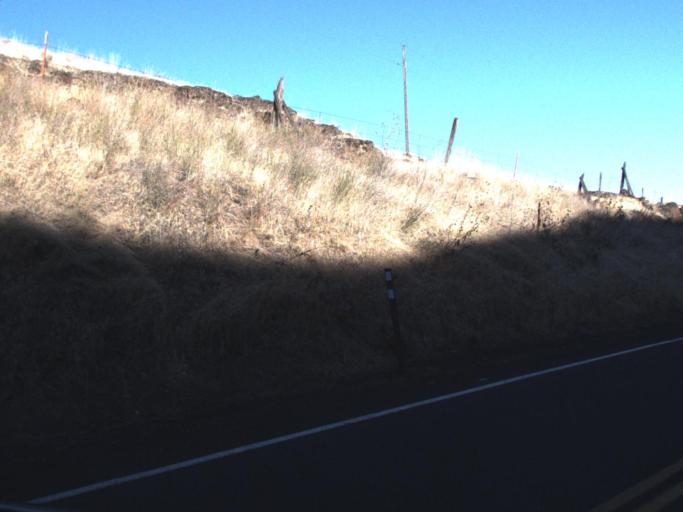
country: US
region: Washington
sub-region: Walla Walla County
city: Waitsburg
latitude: 46.6709
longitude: -118.3152
